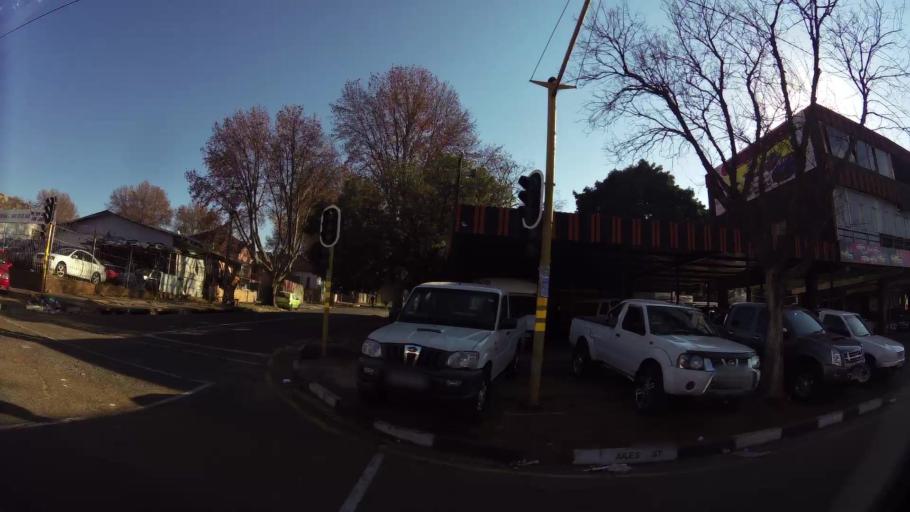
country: ZA
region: Gauteng
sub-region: City of Johannesburg Metropolitan Municipality
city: Johannesburg
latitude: -26.2050
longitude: 28.0827
